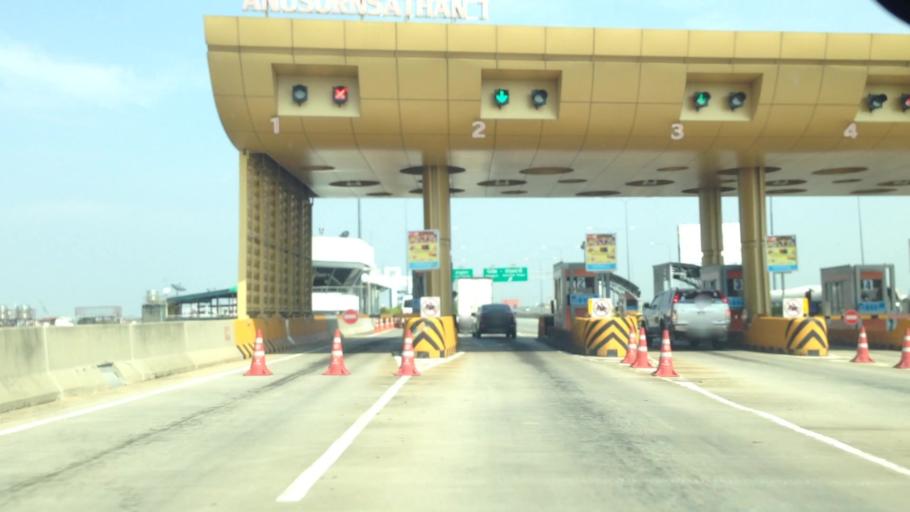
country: TH
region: Bangkok
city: Don Mueang
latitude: 13.9400
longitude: 100.6125
